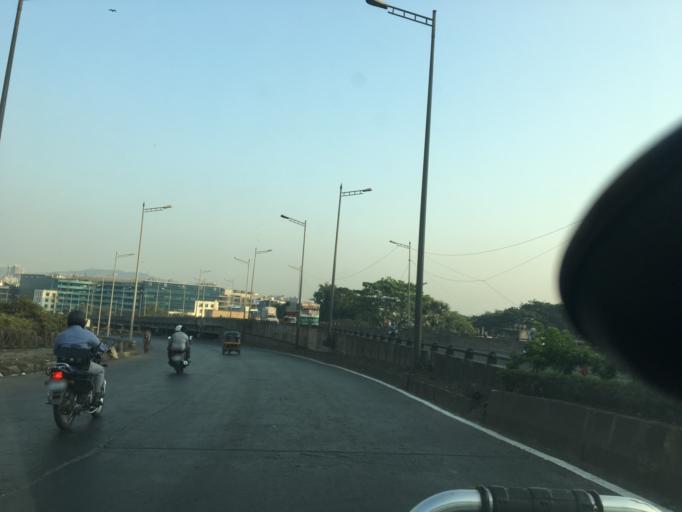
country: IN
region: Maharashtra
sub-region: Mumbai Suburban
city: Powai
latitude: 19.1313
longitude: 72.8751
